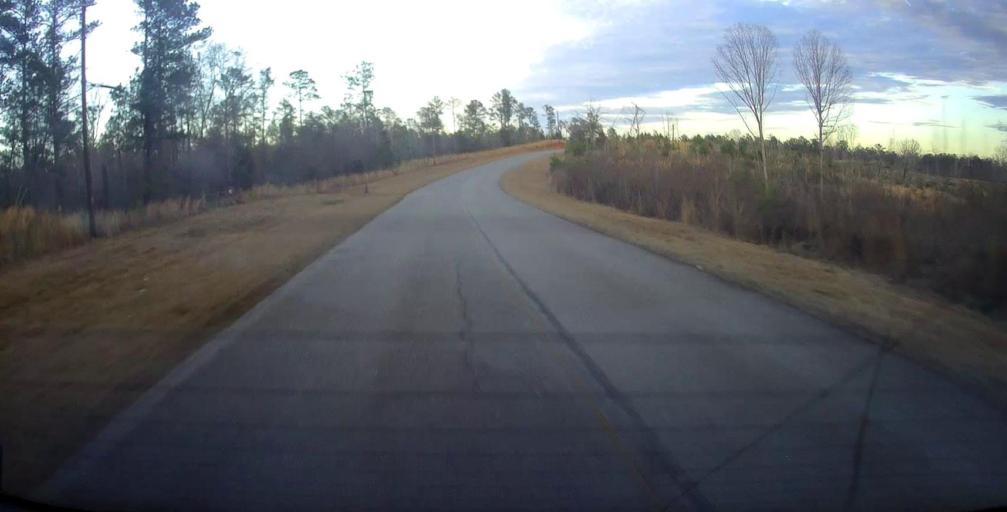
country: US
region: Georgia
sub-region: Harris County
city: Hamilton
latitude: 32.6152
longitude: -84.8329
